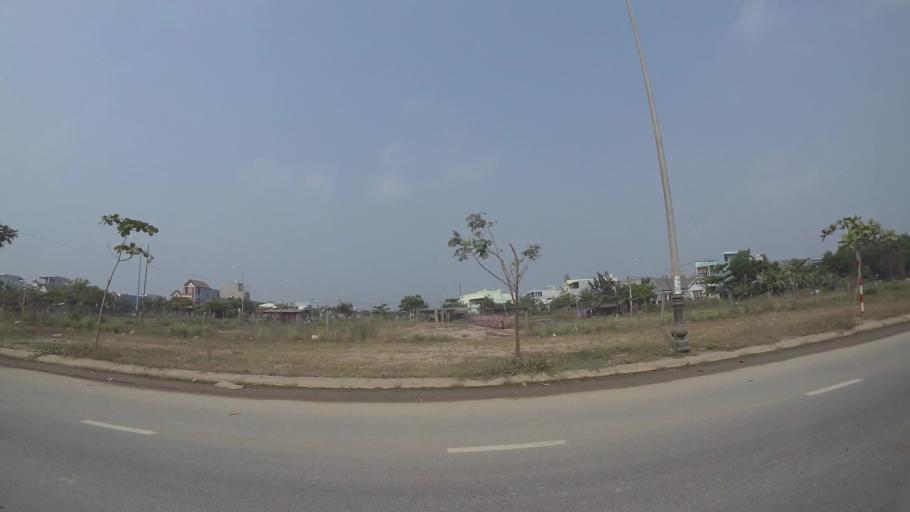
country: VN
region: Da Nang
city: Cam Le
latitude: 15.9953
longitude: 108.2163
